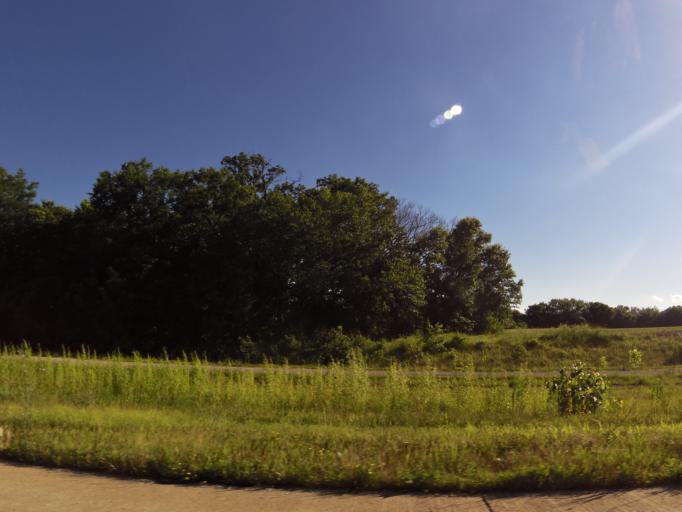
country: US
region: Missouri
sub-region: Ralls County
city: New London
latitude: 39.5440
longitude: -91.3735
